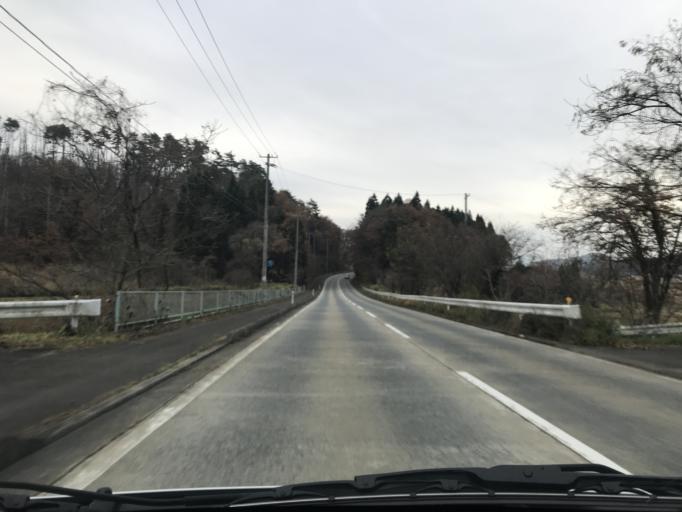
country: JP
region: Iwate
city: Kitakami
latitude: 39.2959
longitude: 141.2104
